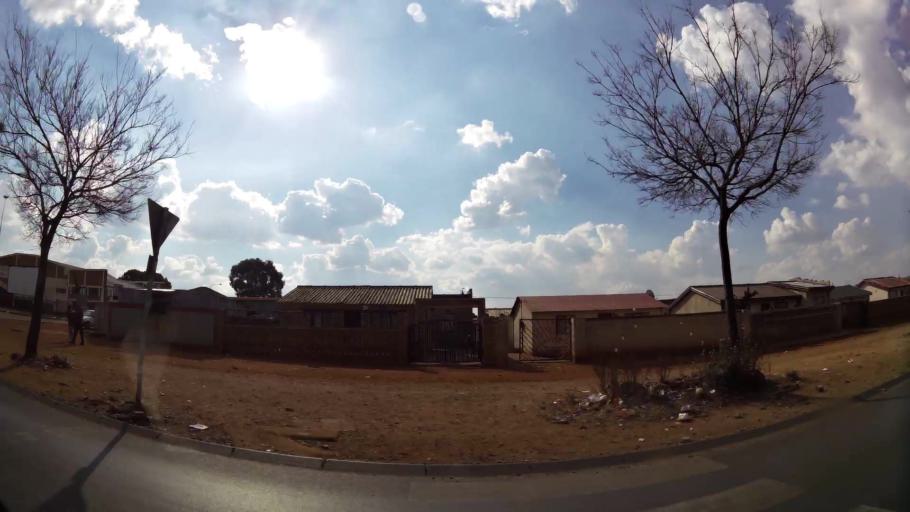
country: ZA
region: Gauteng
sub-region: City of Johannesburg Metropolitan Municipality
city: Soweto
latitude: -26.2232
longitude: 27.8667
